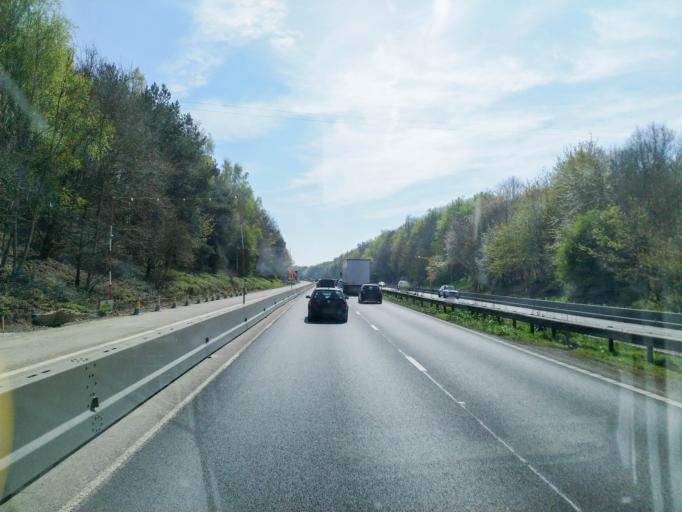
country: GB
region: England
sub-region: Kent
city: Wye
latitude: 51.1292
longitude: 0.9284
